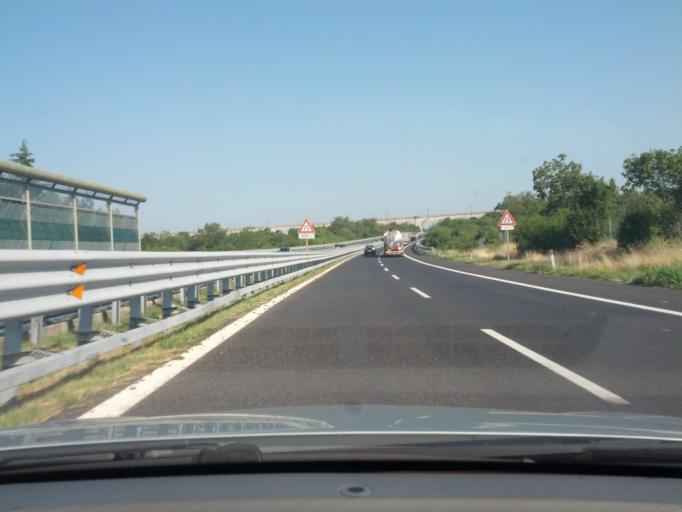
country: IT
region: Friuli Venezia Giulia
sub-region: Provincia di Trieste
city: Aurisina
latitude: 45.7511
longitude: 13.6776
